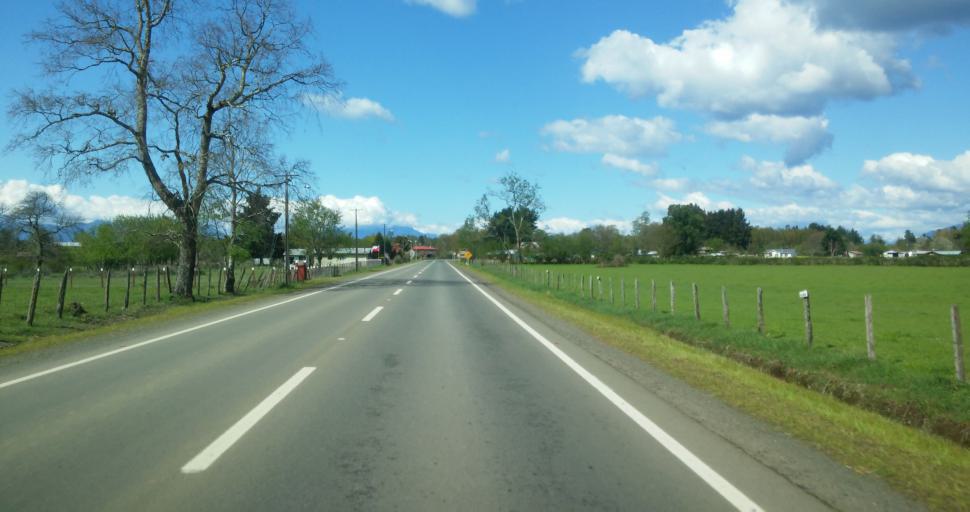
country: CL
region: Los Rios
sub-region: Provincia del Ranco
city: Rio Bueno
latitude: -40.2395
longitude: -72.5970
